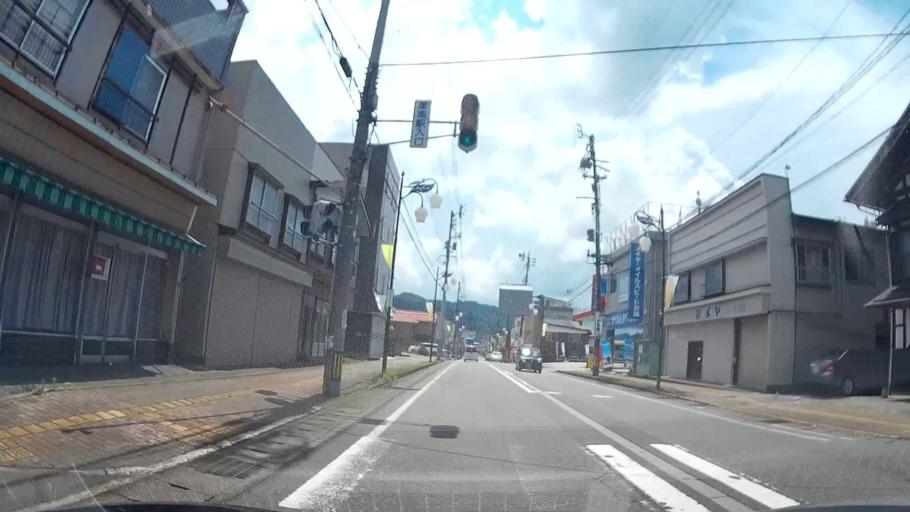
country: JP
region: Niigata
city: Tokamachi
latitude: 37.0156
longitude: 138.6532
